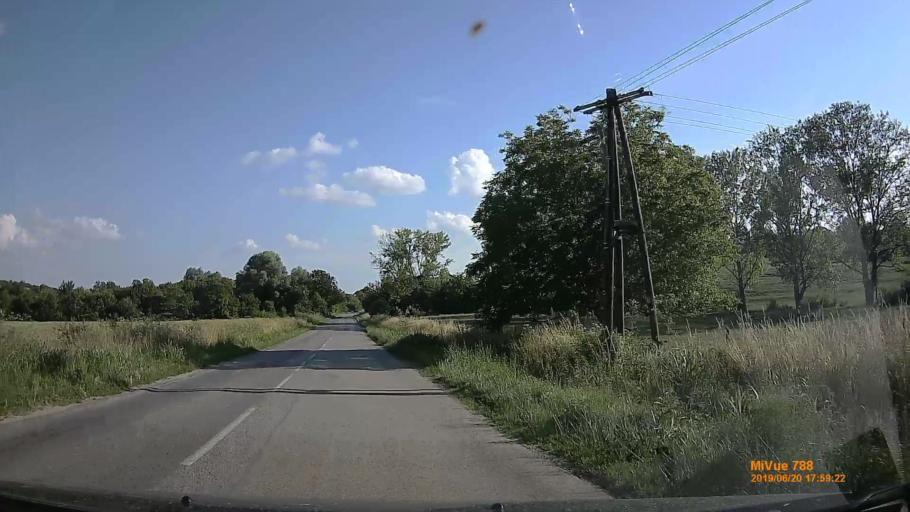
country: HU
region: Baranya
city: Buekkoesd
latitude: 46.0978
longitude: 17.9863
